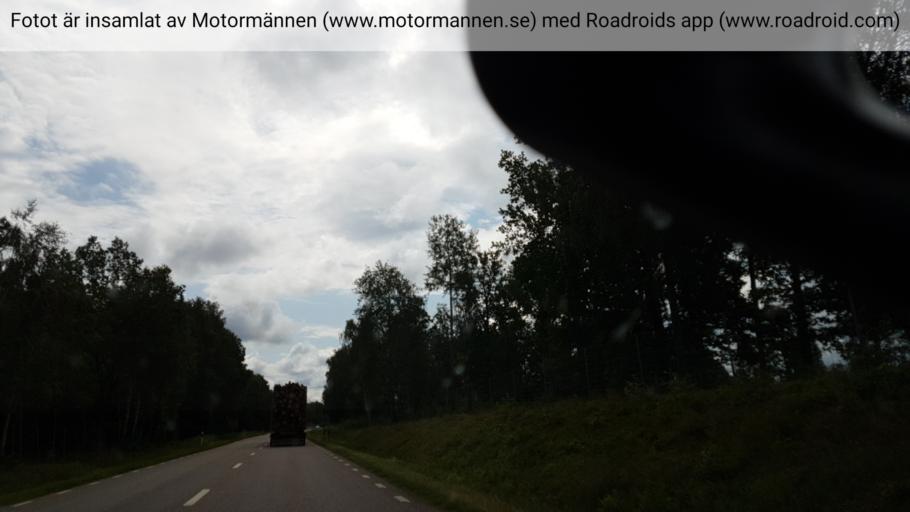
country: SE
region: Vaestra Goetaland
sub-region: Falkopings Kommun
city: Floby
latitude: 58.1906
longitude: 13.3457
